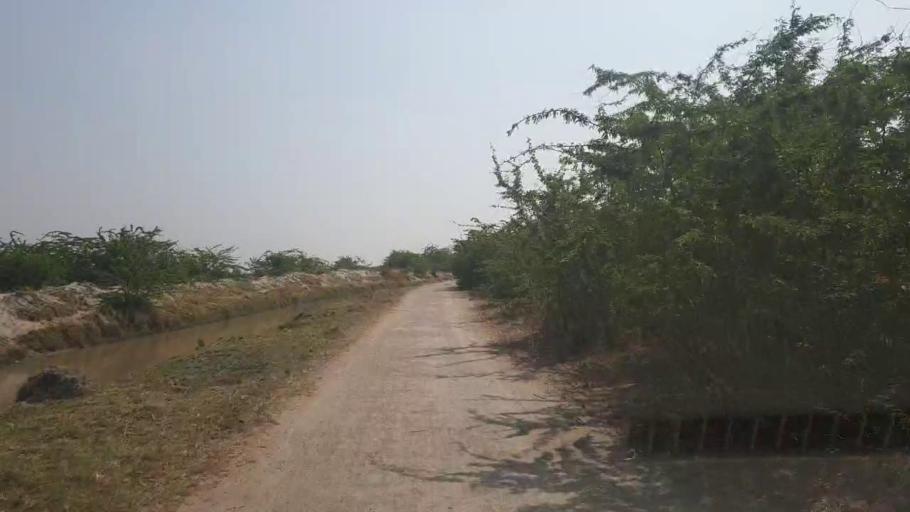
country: PK
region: Sindh
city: Dhoro Naro
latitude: 25.5167
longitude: 69.5403
